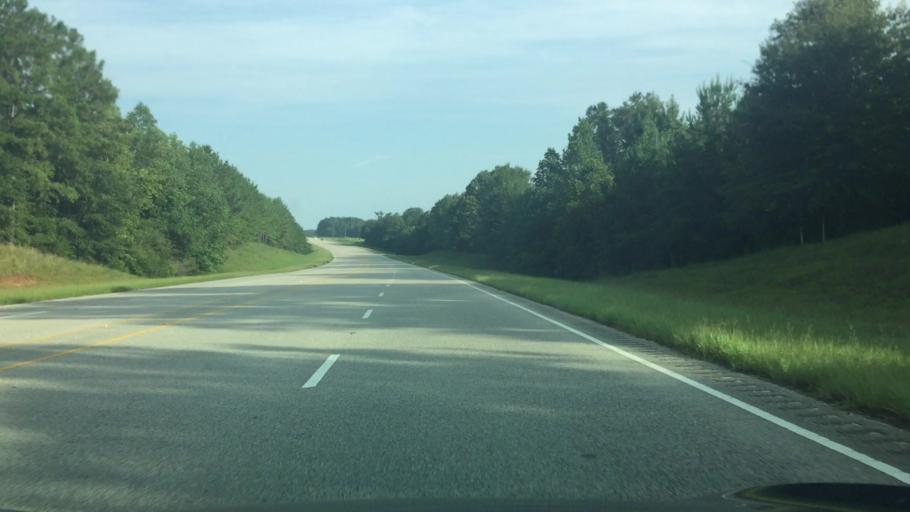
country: US
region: Alabama
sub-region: Butler County
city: Georgiana
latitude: 31.4950
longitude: -86.6892
